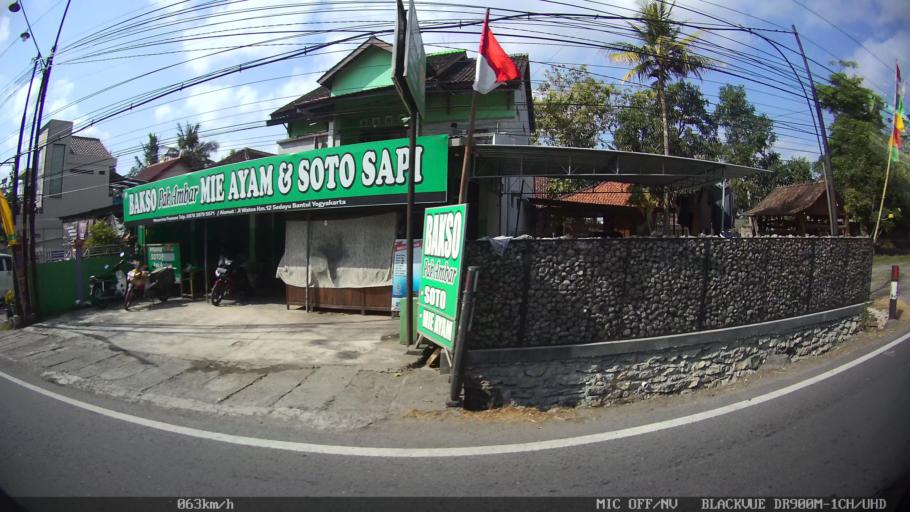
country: ID
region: Daerah Istimewa Yogyakarta
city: Godean
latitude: -7.8139
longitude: 110.2596
